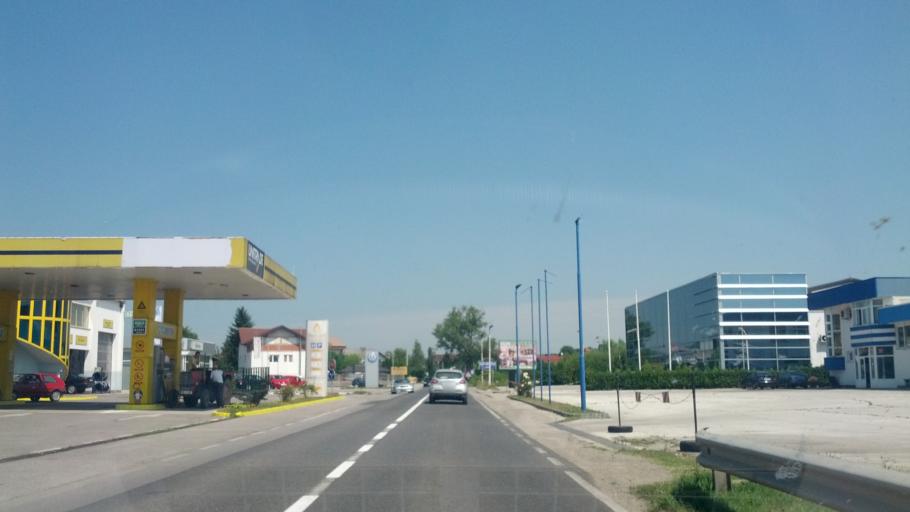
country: BA
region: Federation of Bosnia and Herzegovina
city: Bihac
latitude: 44.8348
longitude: 15.8321
